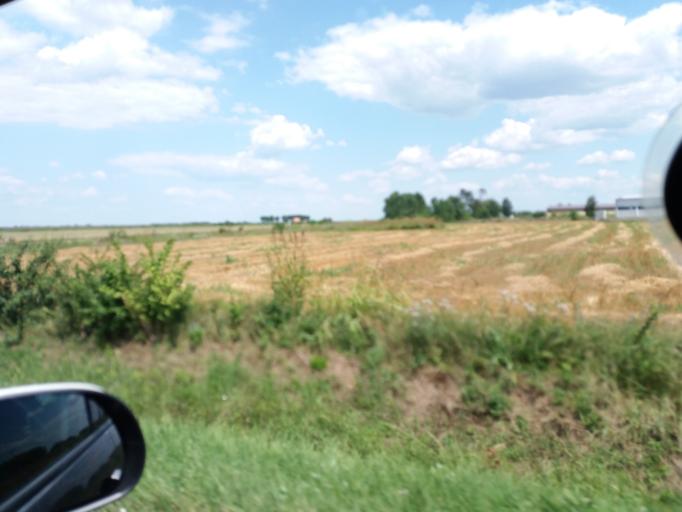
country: RS
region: Autonomna Pokrajina Vojvodina
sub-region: Sremski Okrug
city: Pecinci
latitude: 44.8627
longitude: 19.9599
